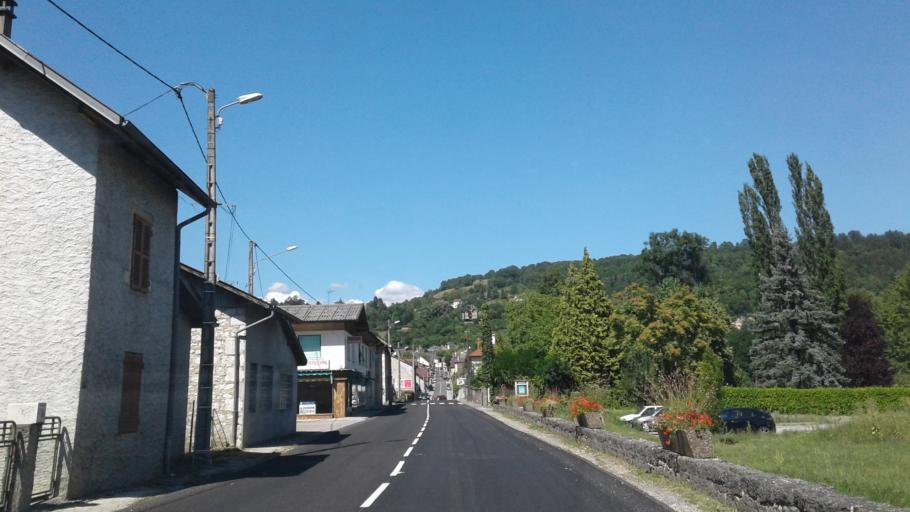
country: FR
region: Rhone-Alpes
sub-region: Departement de l'Ain
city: Artemare
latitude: 45.8702
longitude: 5.6906
